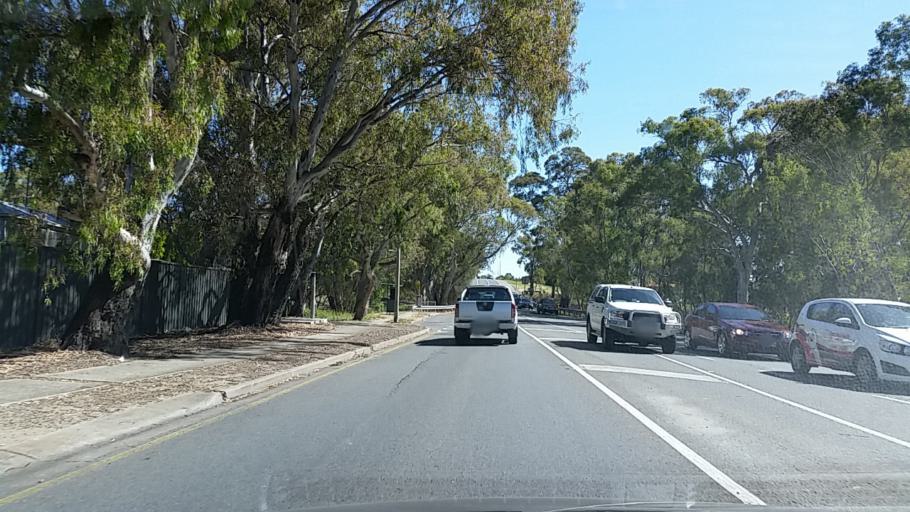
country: AU
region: South Australia
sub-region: Tea Tree Gully
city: Golden Grove
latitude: -34.7958
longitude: 138.7086
